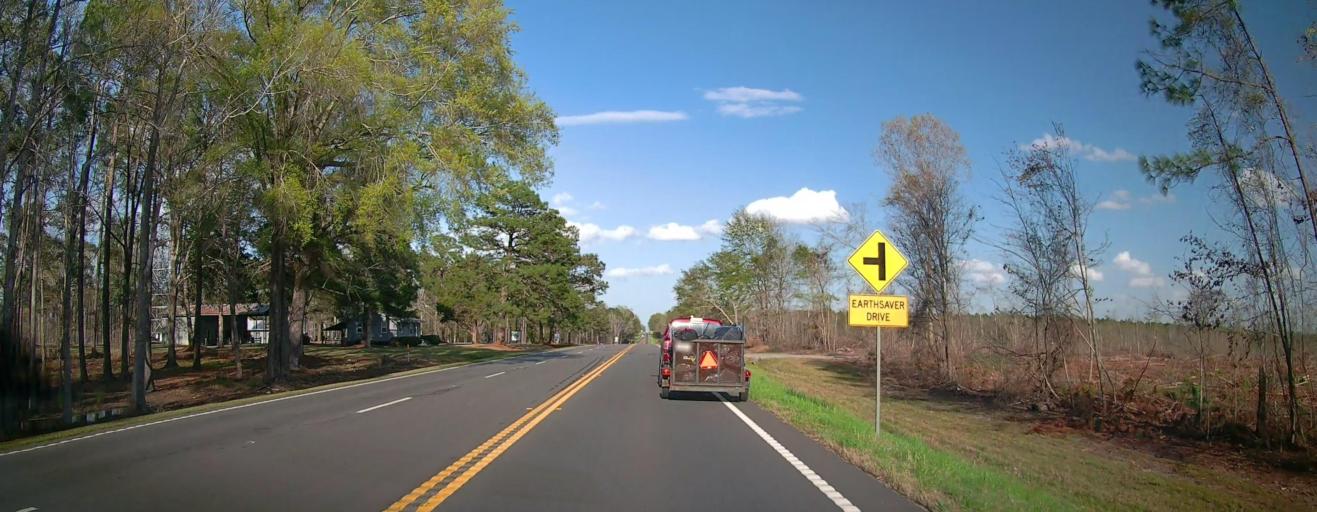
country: US
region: Georgia
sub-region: Montgomery County
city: Mount Vernon
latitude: 32.1923
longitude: -82.5170
